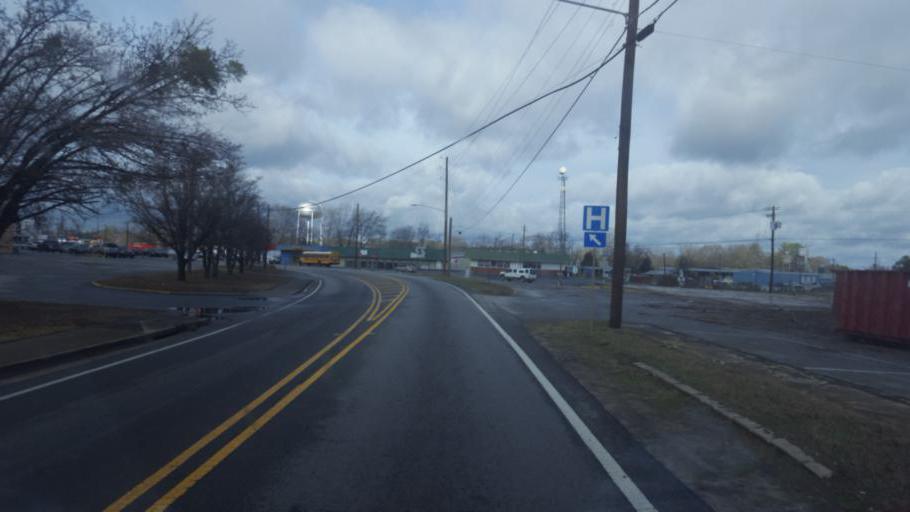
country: US
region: Georgia
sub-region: Butts County
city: Jackson
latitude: 33.2937
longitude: -83.9534
